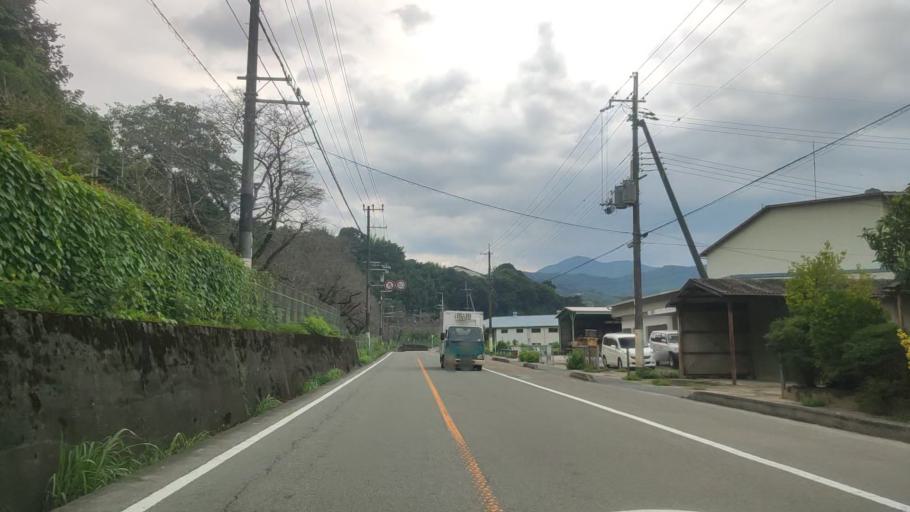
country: JP
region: Wakayama
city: Hashimoto
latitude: 34.2910
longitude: 135.5716
